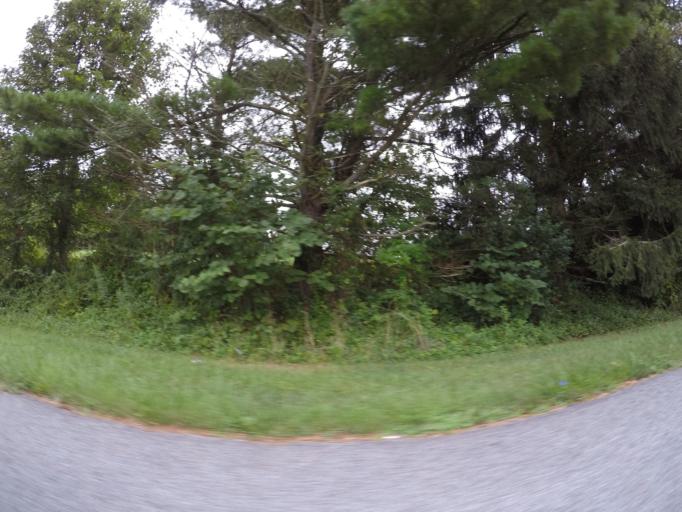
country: US
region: Maryland
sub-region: Carroll County
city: Sykesville
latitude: 39.3382
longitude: -77.0486
